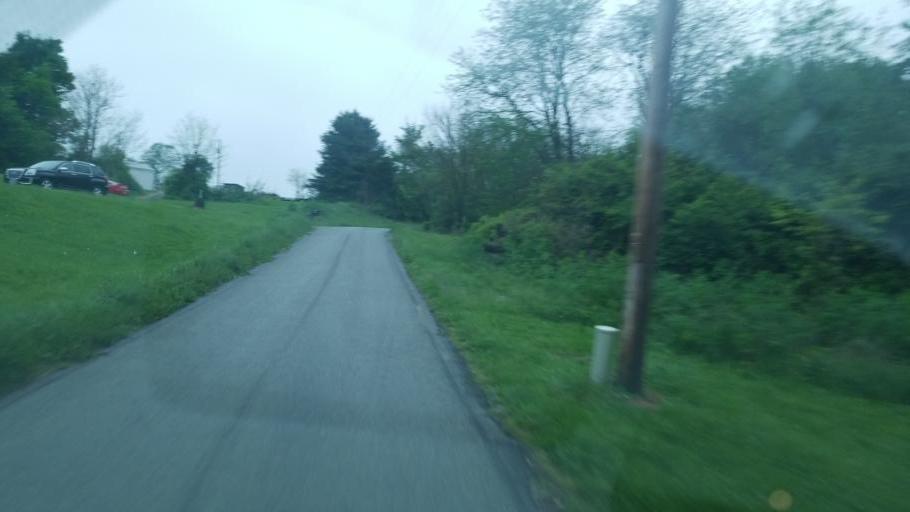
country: US
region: Ohio
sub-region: Highland County
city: Hillsboro
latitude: 39.1770
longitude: -83.6451
